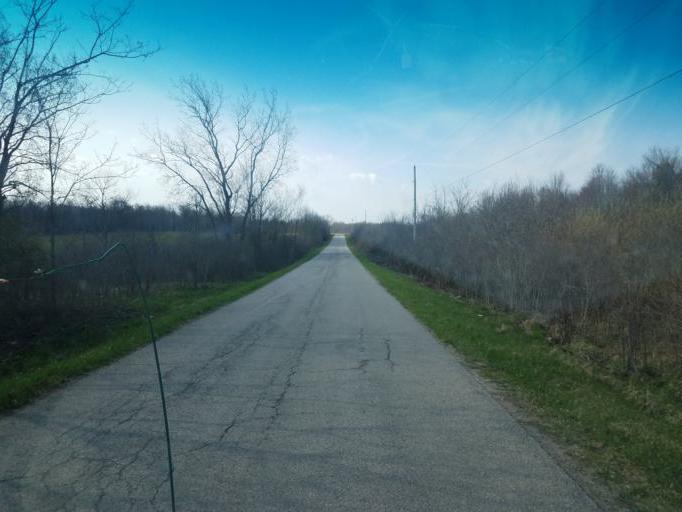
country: US
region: Ohio
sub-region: Richland County
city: Lincoln Heights
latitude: 40.8324
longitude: -82.5005
